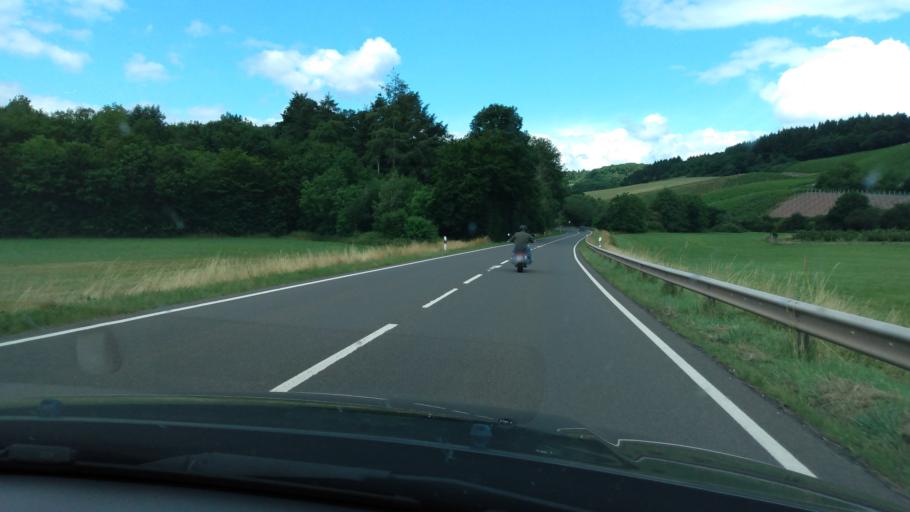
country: DE
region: Rheinland-Pfalz
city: Wittlich
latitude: 49.9898
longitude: 6.8715
